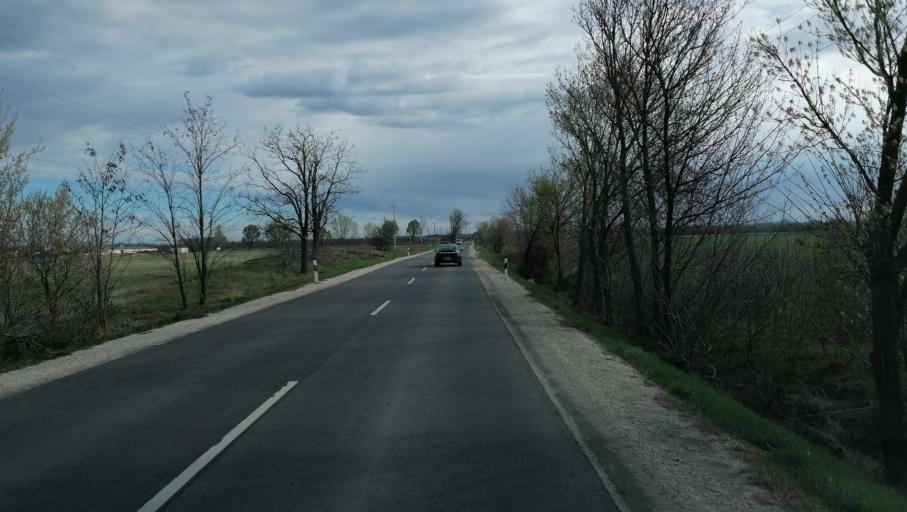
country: HU
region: Pest
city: Bugyi
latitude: 47.2464
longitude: 19.2001
